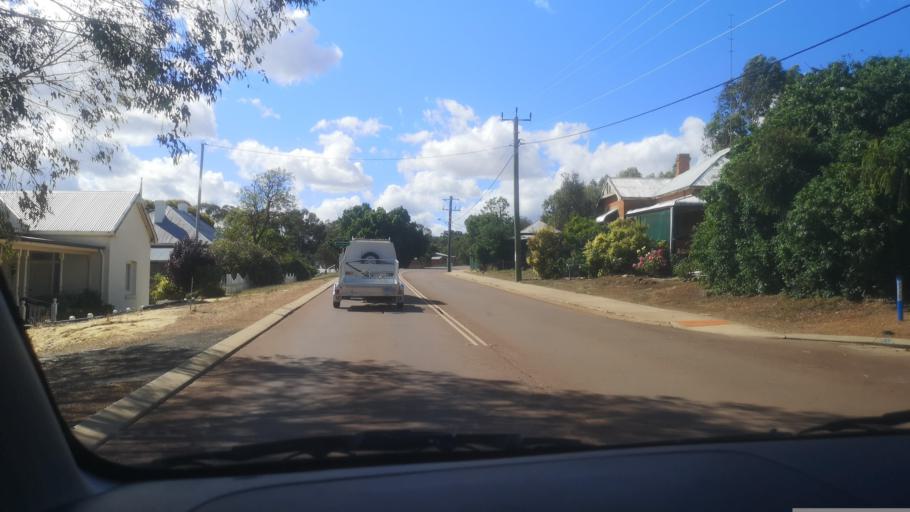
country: AU
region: Western Australia
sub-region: Toodyay
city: Toodyay
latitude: -31.5479
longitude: 116.4617
